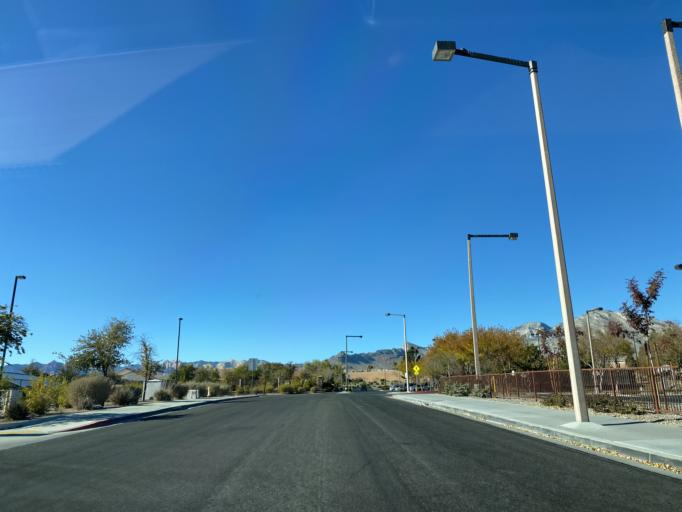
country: US
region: Nevada
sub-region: Clark County
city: Summerlin South
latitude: 36.1683
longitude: -115.3446
